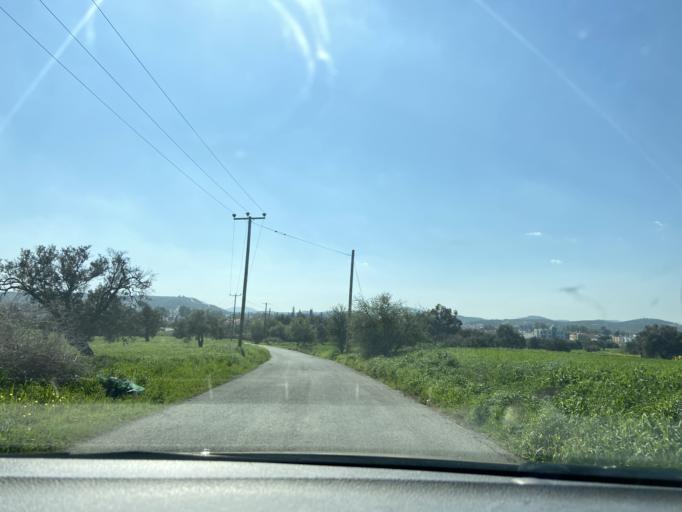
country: CY
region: Lefkosia
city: Dali
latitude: 35.0273
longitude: 33.3907
